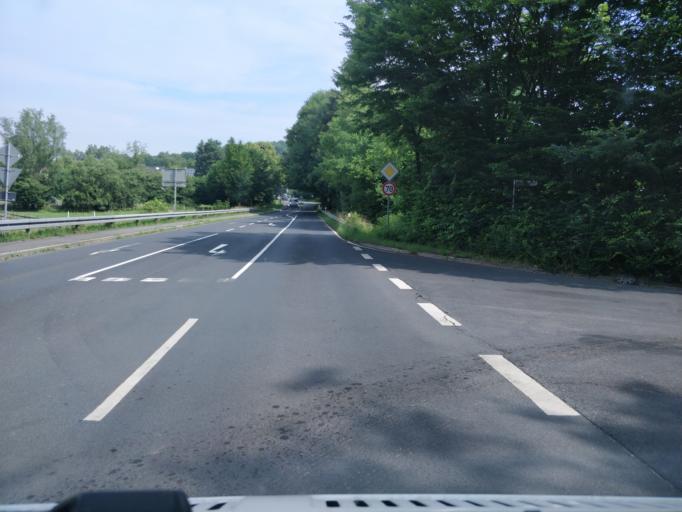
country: DE
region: North Rhine-Westphalia
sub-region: Regierungsbezirk Koln
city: Numbrecht
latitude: 50.9234
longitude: 7.5759
